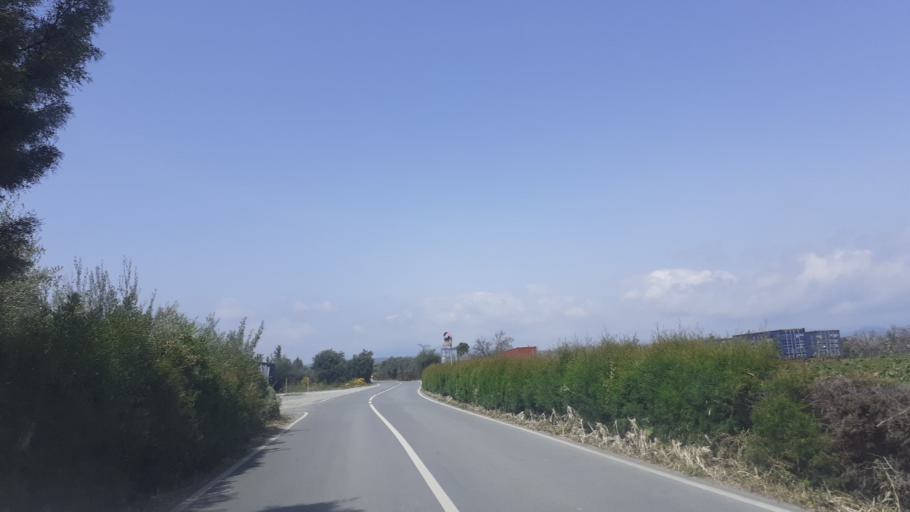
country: CY
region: Limassol
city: Ypsonas
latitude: 34.6671
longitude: 32.9616
